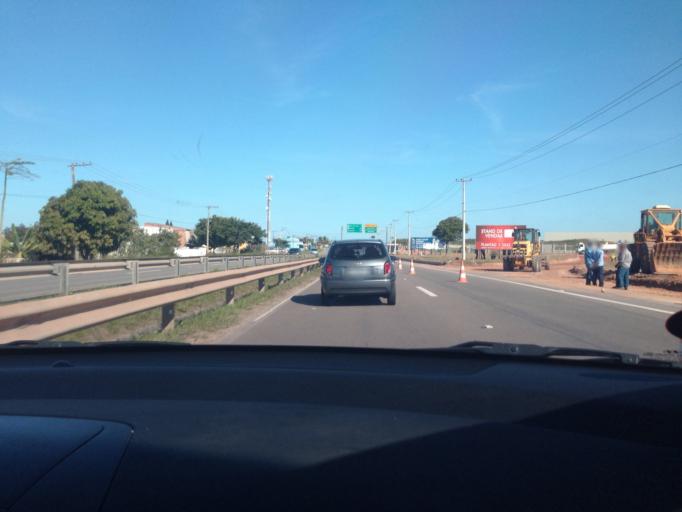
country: BR
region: Espirito Santo
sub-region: Vitoria
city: Vitoria
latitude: -20.4797
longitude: -40.3530
